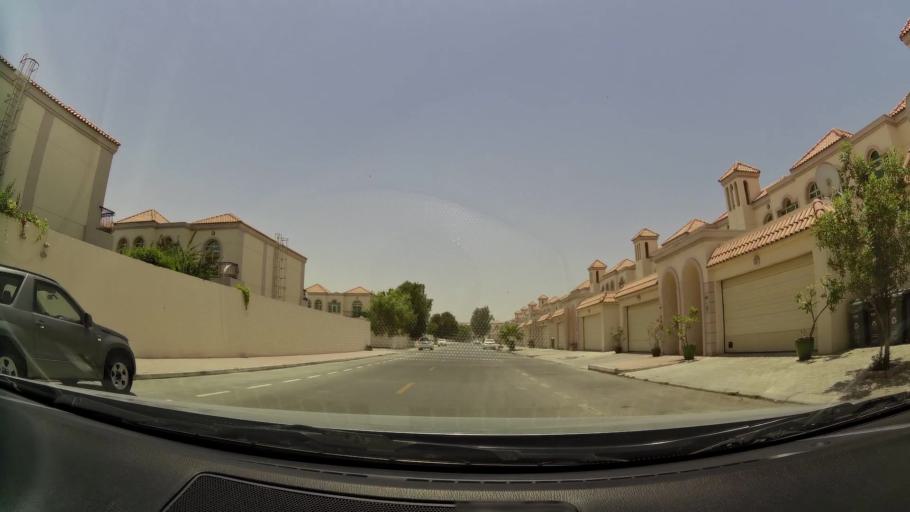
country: AE
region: Dubai
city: Dubai
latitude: 25.1723
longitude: 55.2404
